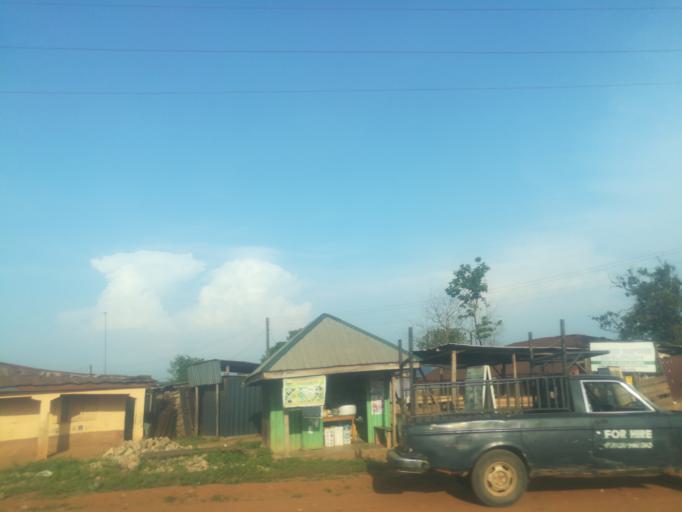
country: NG
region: Oyo
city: Moniya
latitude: 7.5637
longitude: 3.8859
